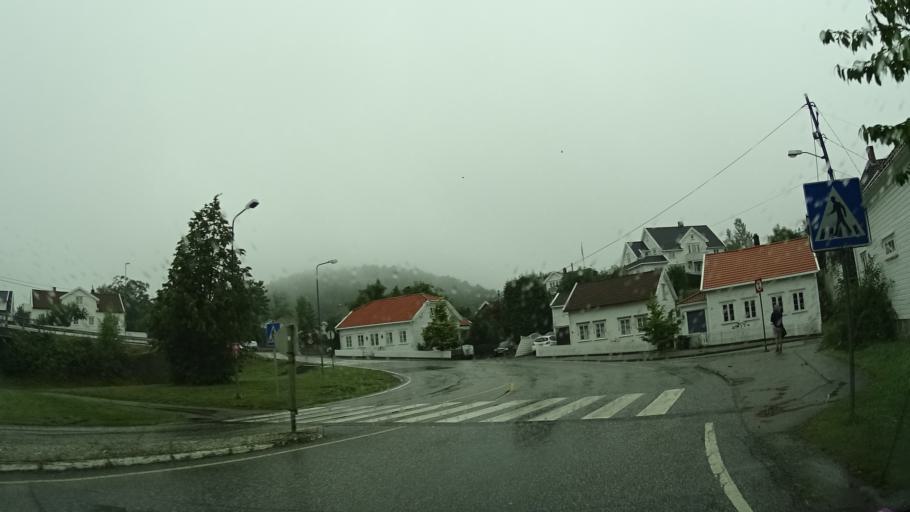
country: NO
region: Aust-Agder
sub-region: Lillesand
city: Lillesand
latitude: 58.2524
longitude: 8.3728
